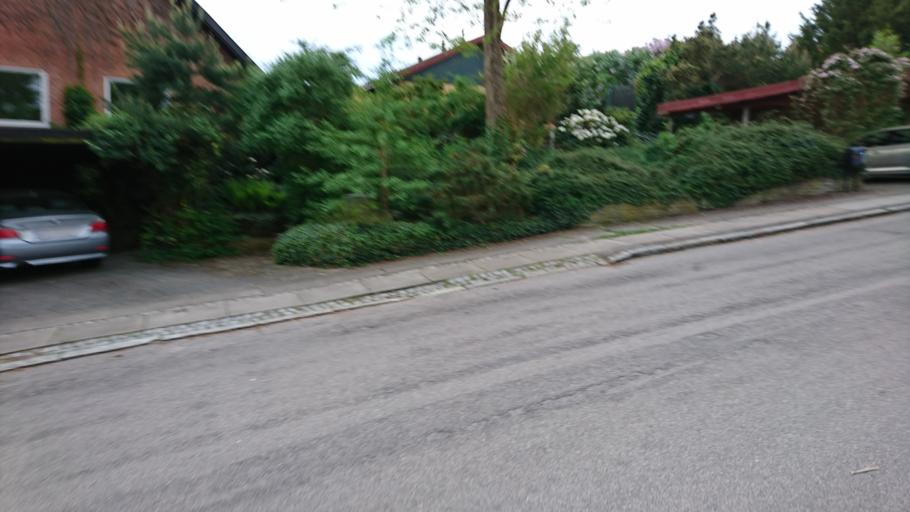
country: DK
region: Capital Region
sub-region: Ballerup Kommune
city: Ballerup
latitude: 55.7522
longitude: 12.3995
